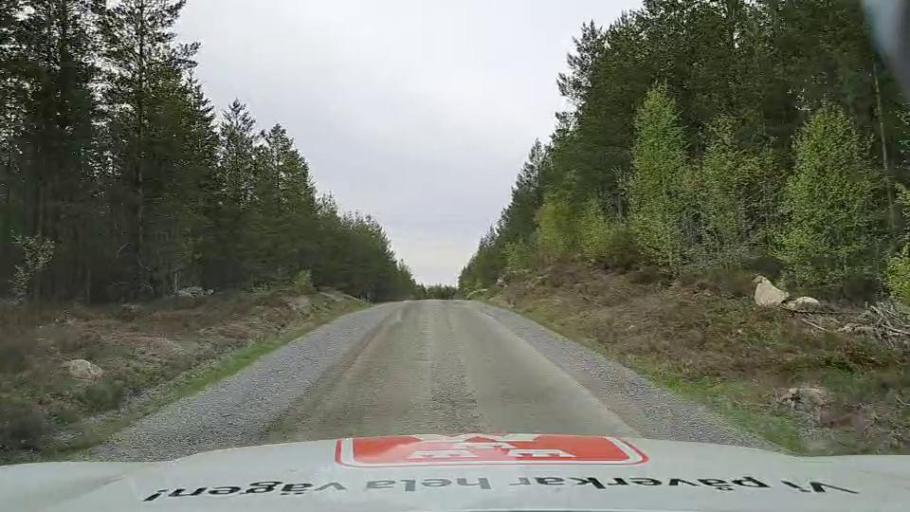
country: SE
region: Jaemtland
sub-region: Braecke Kommun
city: Braecke
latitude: 62.4672
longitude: 14.9179
